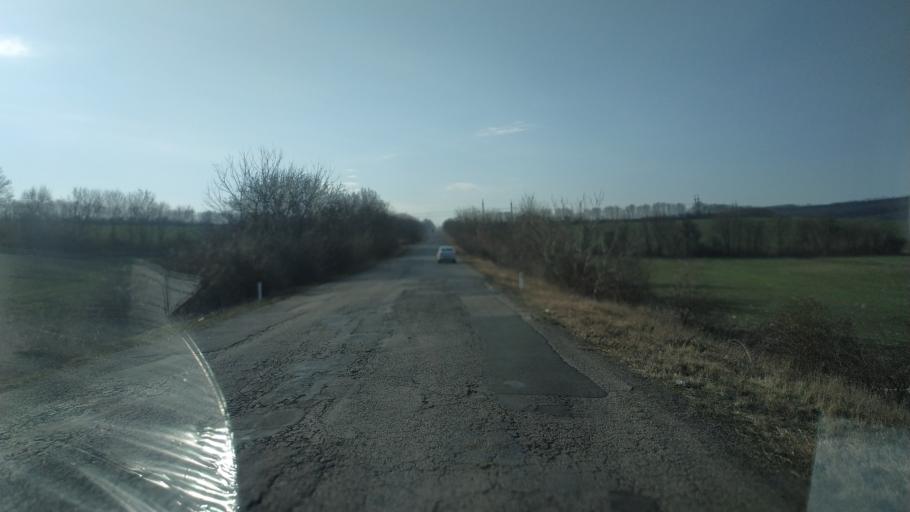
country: MD
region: Chisinau
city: Singera
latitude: 46.8791
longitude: 29.0394
